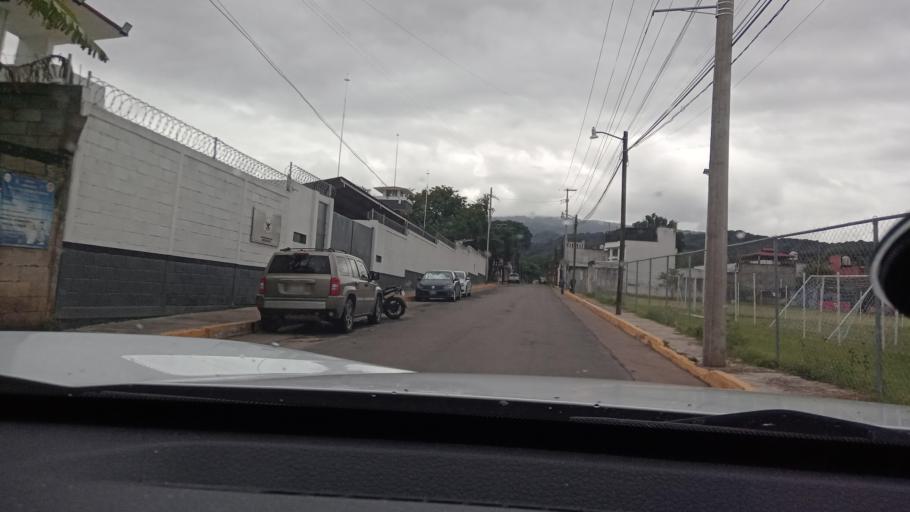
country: MX
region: Veracruz
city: Coatepec
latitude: 19.4524
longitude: -96.9761
